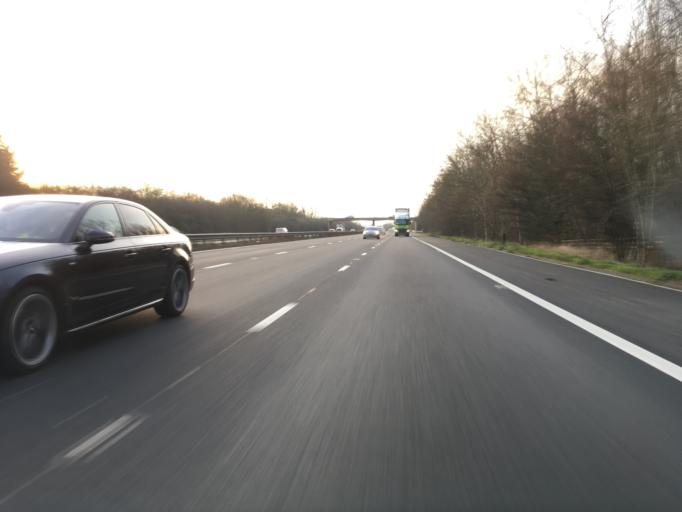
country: GB
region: England
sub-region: Gloucestershire
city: Uckington
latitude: 51.9527
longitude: -2.1270
